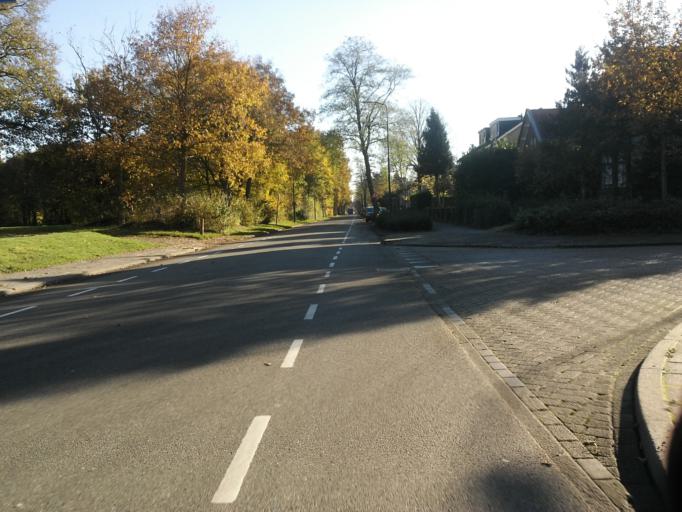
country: NL
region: Utrecht
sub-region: Gemeente Soest
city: Soest
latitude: 52.1205
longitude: 5.2857
